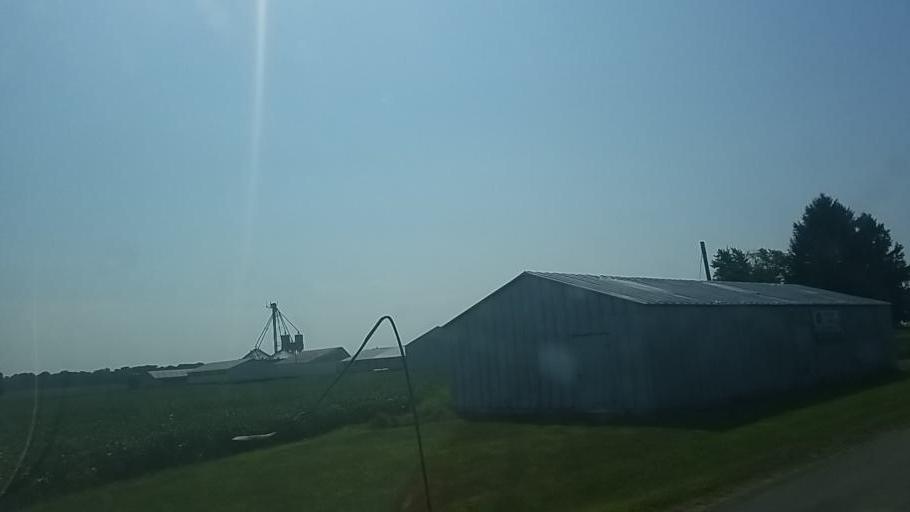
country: US
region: Ohio
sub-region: Marion County
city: Marion
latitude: 40.7170
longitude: -83.1499
